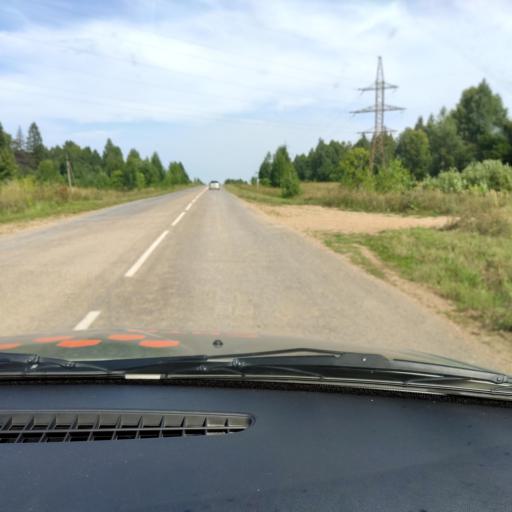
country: RU
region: Bashkortostan
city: Pavlovka
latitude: 55.3894
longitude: 56.5212
